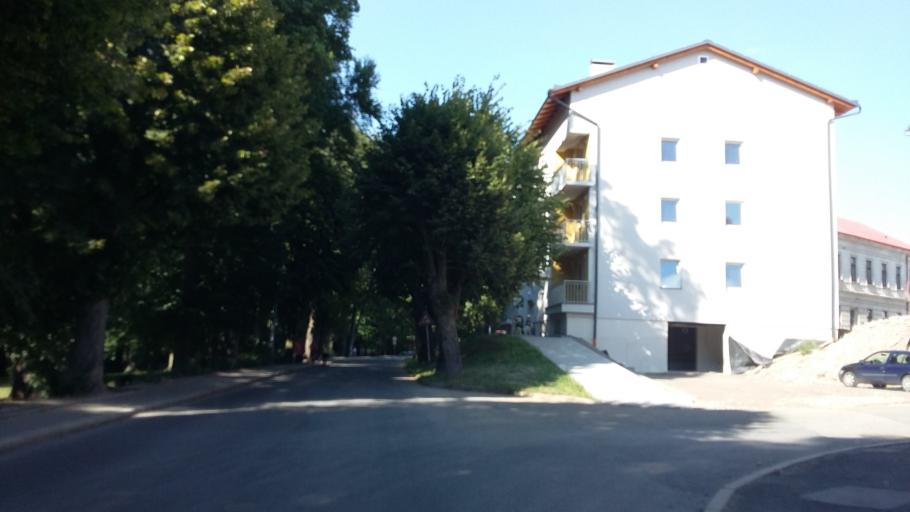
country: CZ
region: Liberecky
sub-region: Okres Semily
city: Turnov
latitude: 50.5952
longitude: 15.1621
